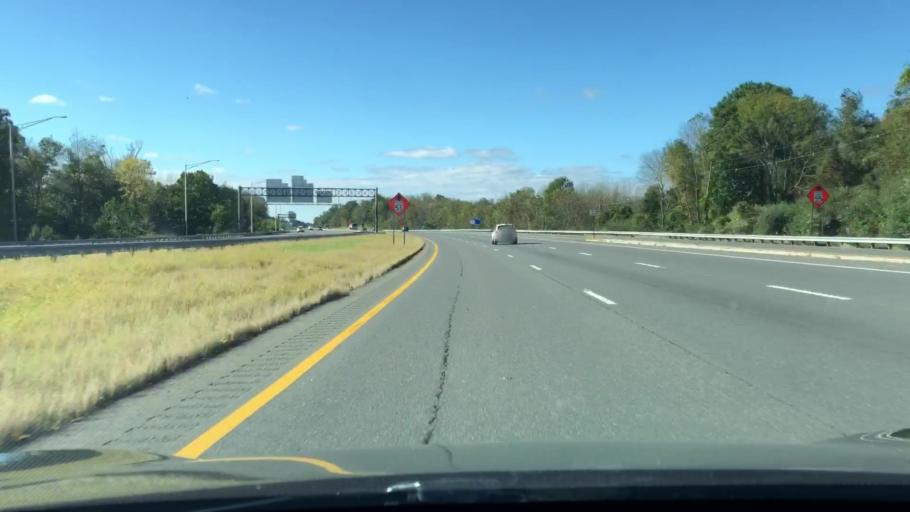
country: US
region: New Jersey
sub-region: Mercer County
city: Ewing
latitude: 40.2873
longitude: -74.8171
